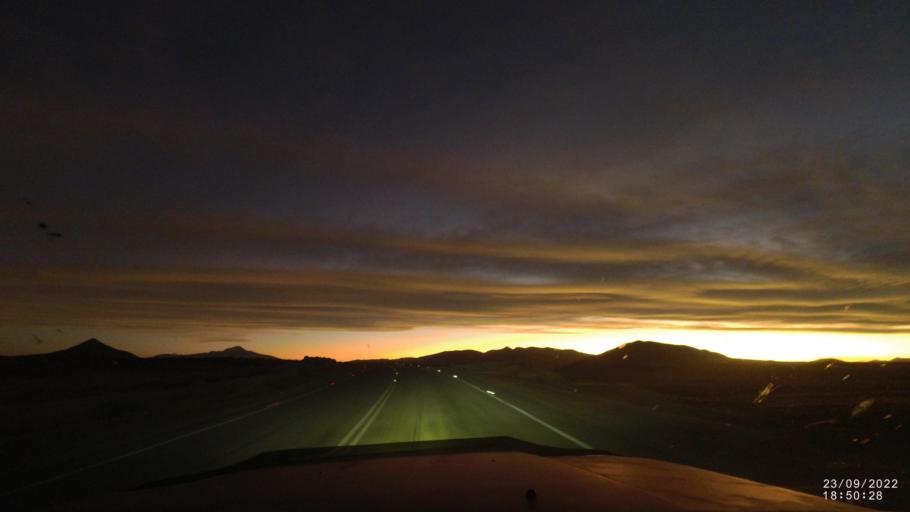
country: BO
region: Oruro
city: Challapata
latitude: -19.4647
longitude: -67.4254
